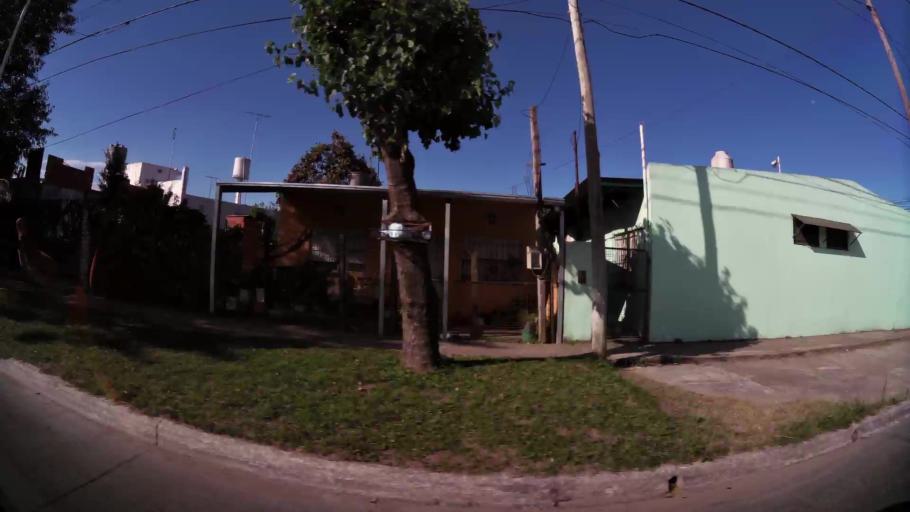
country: AR
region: Buenos Aires
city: Santa Catalina - Dique Lujan
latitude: -34.4897
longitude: -58.7147
